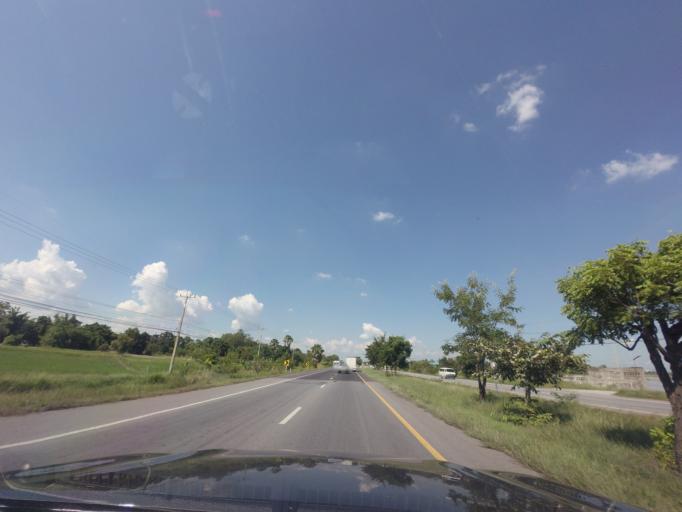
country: TH
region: Nakhon Ratchasima
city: Non Sung
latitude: 15.1641
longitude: 102.3322
